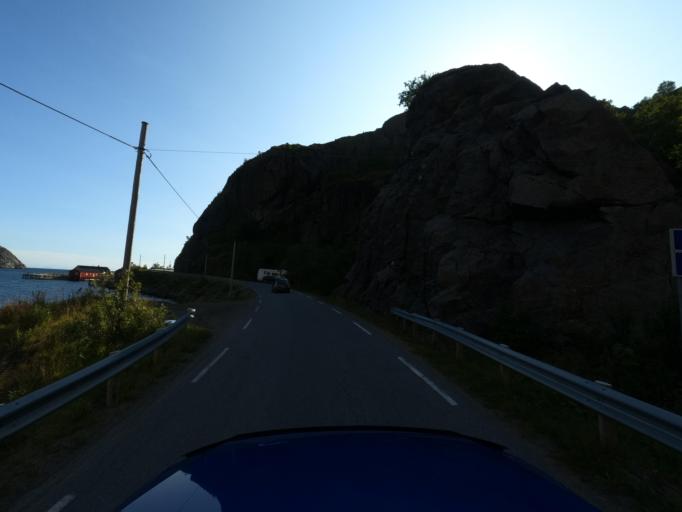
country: NO
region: Nordland
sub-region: Flakstad
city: Ramberg
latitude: 68.0391
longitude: 13.3473
